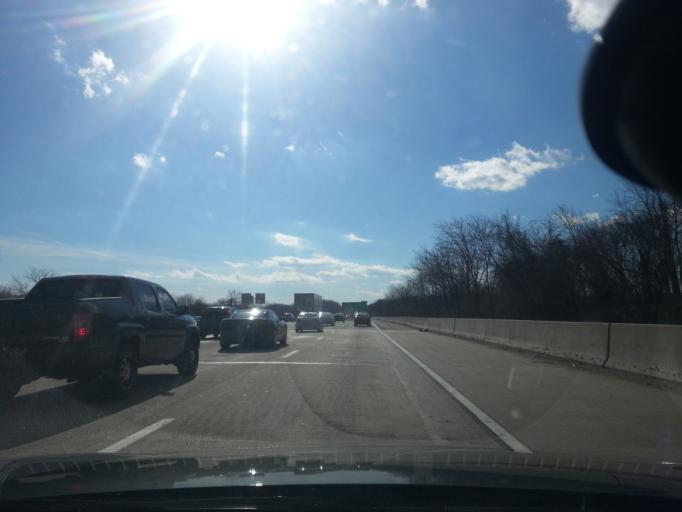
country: US
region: Delaware
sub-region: New Castle County
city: Newport
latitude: 39.6948
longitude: -75.6225
